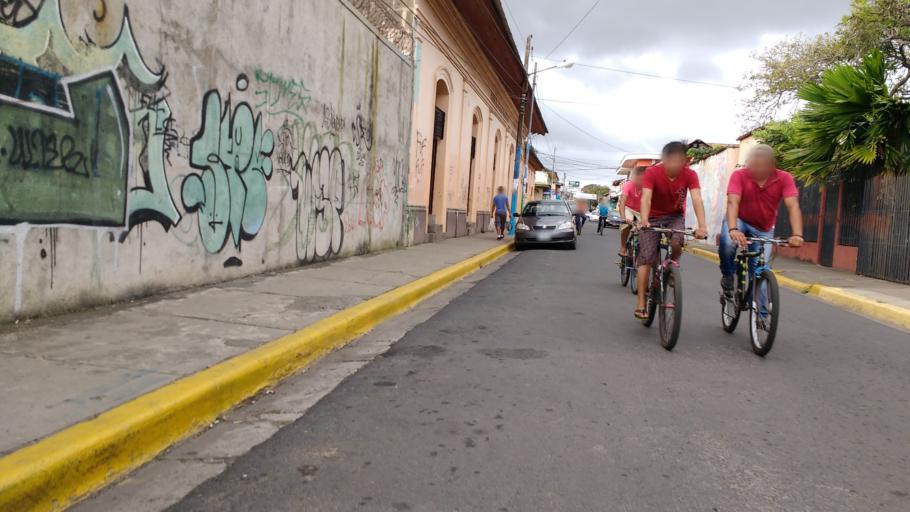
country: NI
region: Carazo
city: Jinotepe
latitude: 11.8497
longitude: -86.2004
